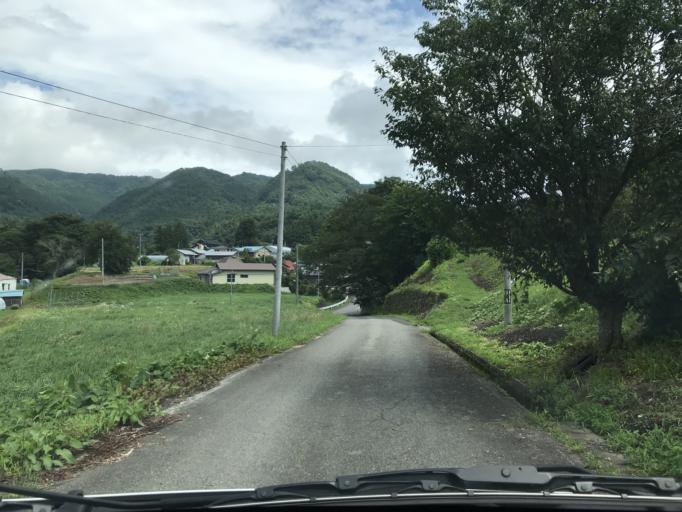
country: JP
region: Iwate
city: Mizusawa
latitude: 39.0609
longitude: 141.3925
